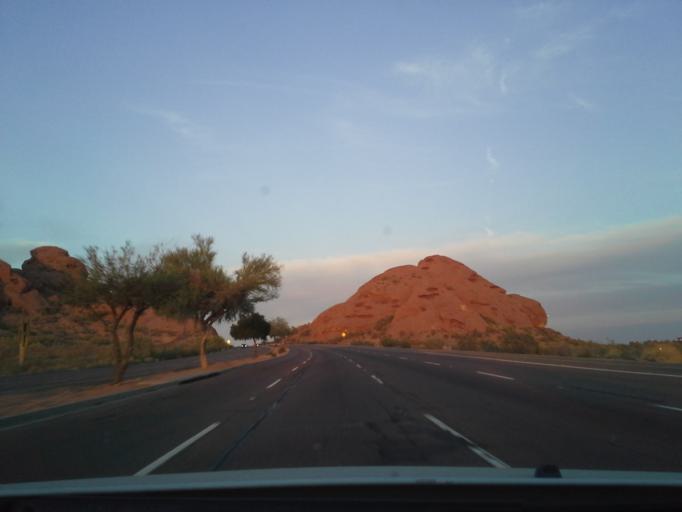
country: US
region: Arizona
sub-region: Maricopa County
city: Tempe Junction
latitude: 33.4654
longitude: -111.9594
